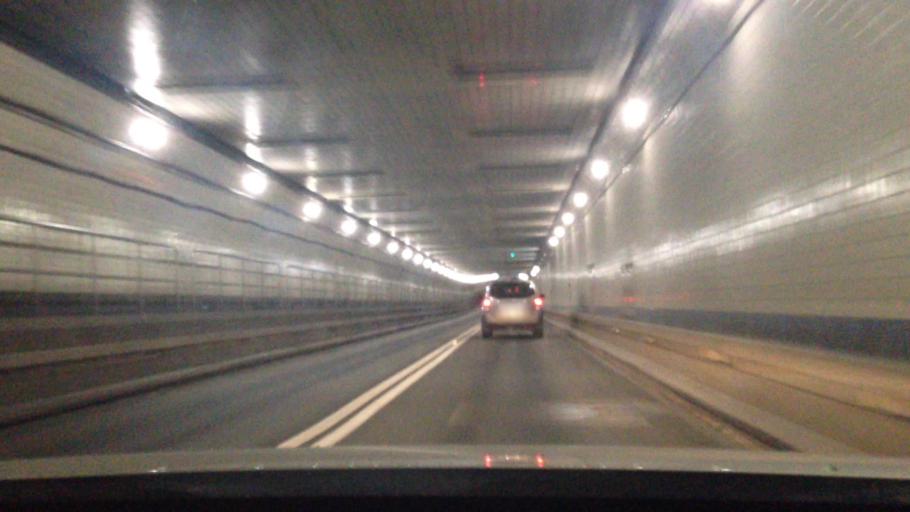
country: US
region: New Jersey
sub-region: Hudson County
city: Weehawken
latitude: 40.7628
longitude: -74.0118
